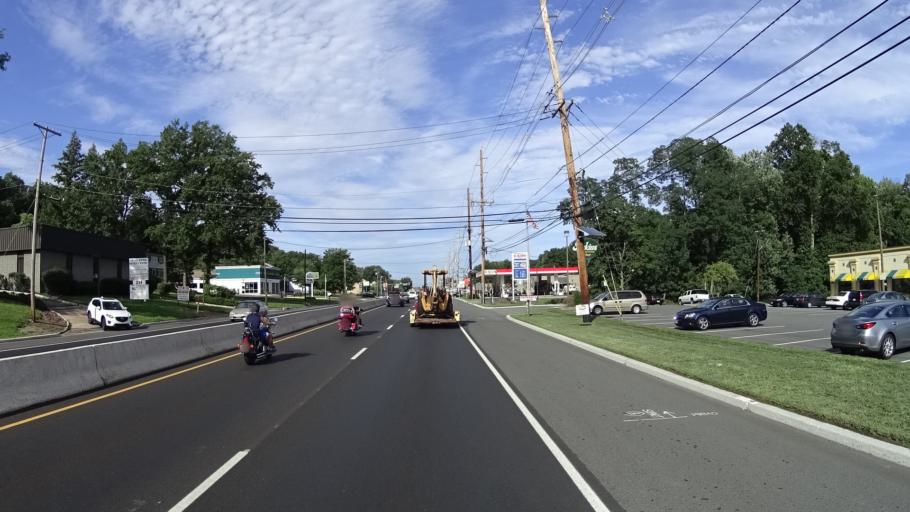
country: US
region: New Jersey
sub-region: Middlesex County
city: Middlesex
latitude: 40.5903
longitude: -74.5004
